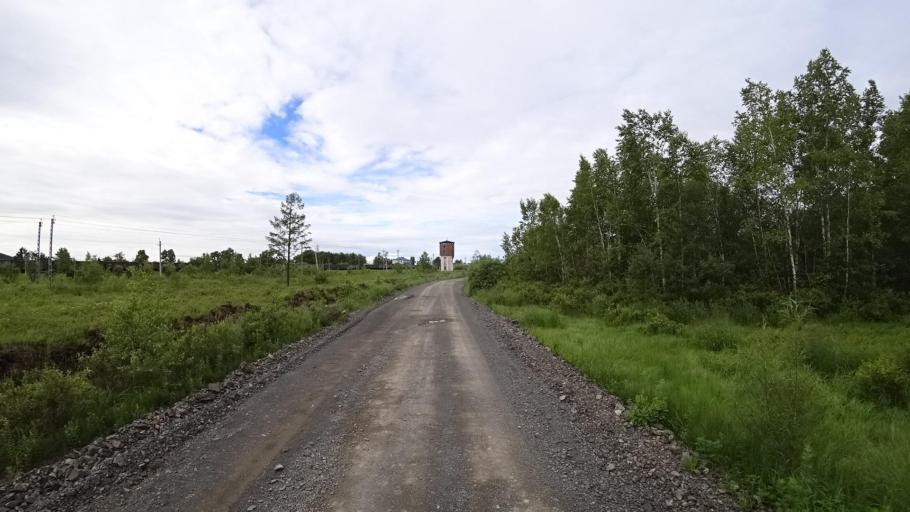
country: RU
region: Khabarovsk Krai
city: Amursk
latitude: 49.9019
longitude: 136.1371
